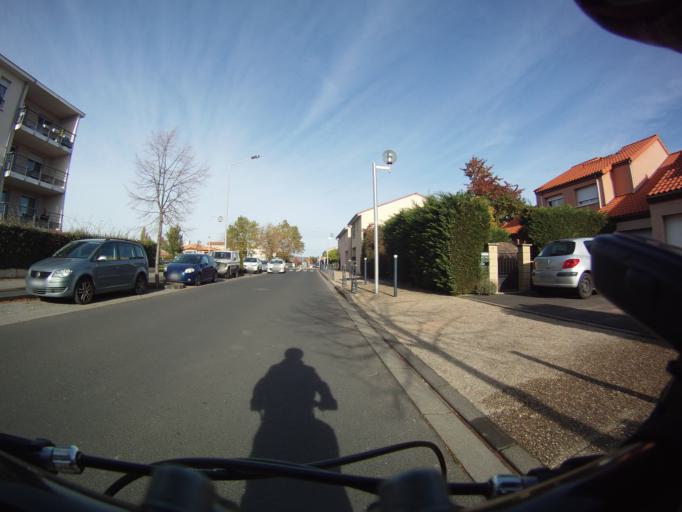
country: FR
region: Auvergne
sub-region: Departement du Puy-de-Dome
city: Aubiere
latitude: 45.7534
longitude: 3.1018
